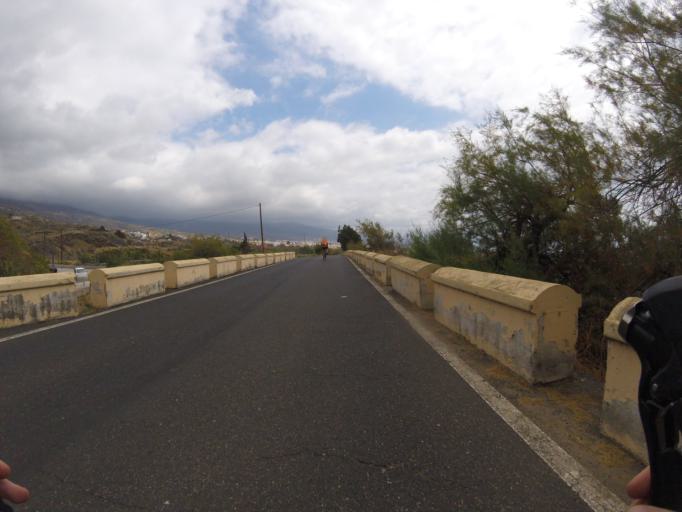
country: ES
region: Canary Islands
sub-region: Provincia de Santa Cruz de Tenerife
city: Guimar
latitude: 28.2986
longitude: -16.4180
